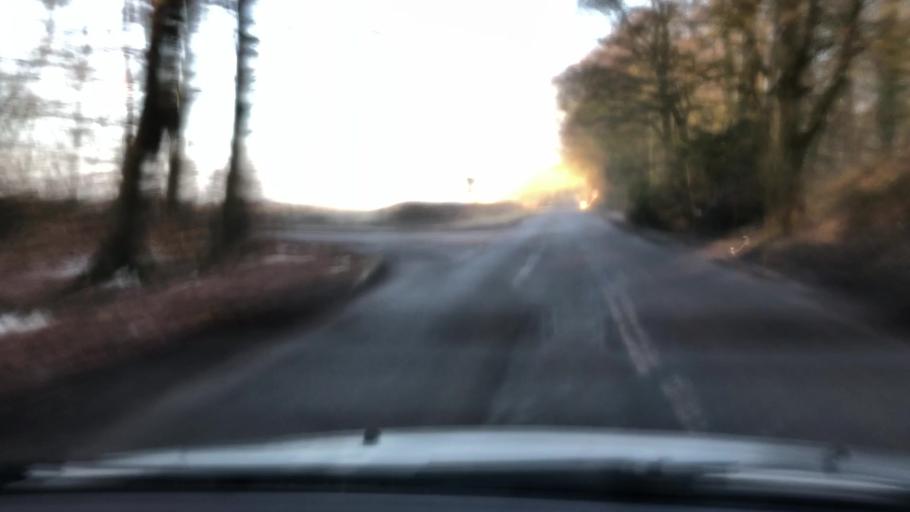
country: GB
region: England
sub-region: Hampshire
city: Alton
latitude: 51.1901
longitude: -1.0150
